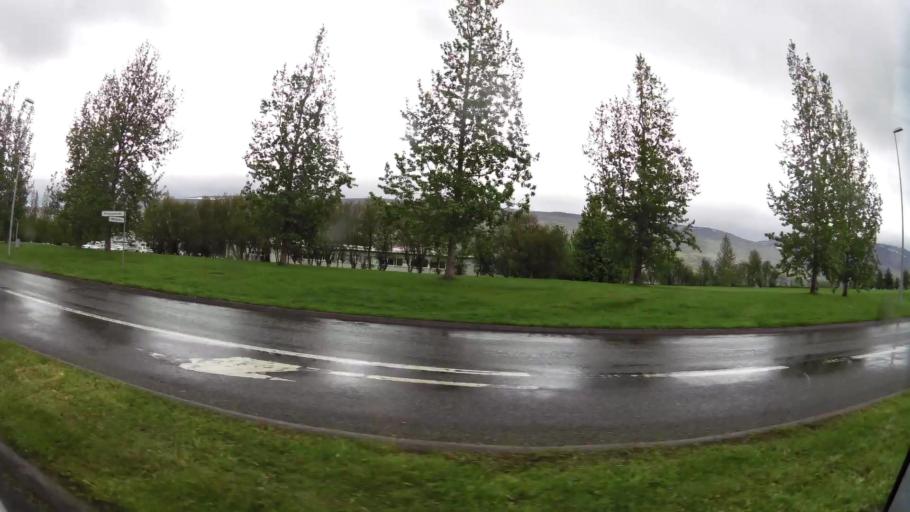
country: IS
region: Northeast
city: Akureyri
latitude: 65.6729
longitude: -18.0966
